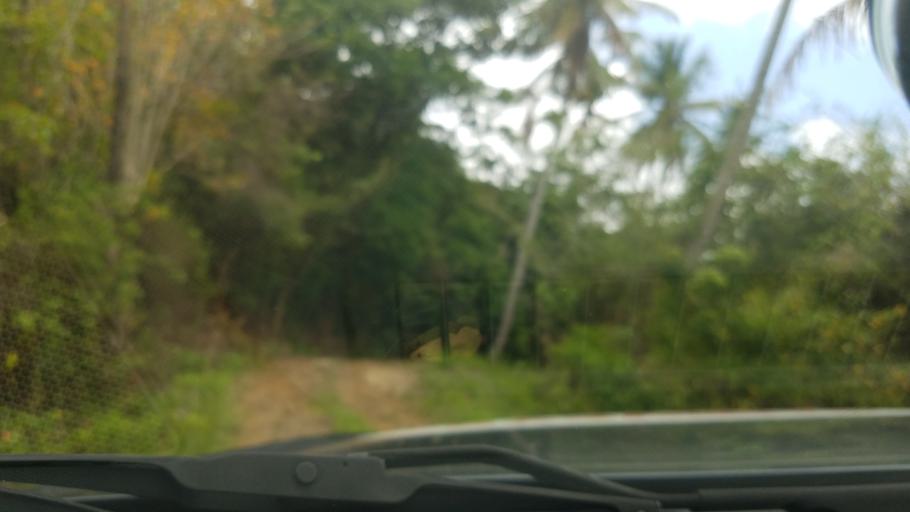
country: LC
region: Gros-Islet
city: Gros Islet
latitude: 14.0641
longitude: -60.9612
